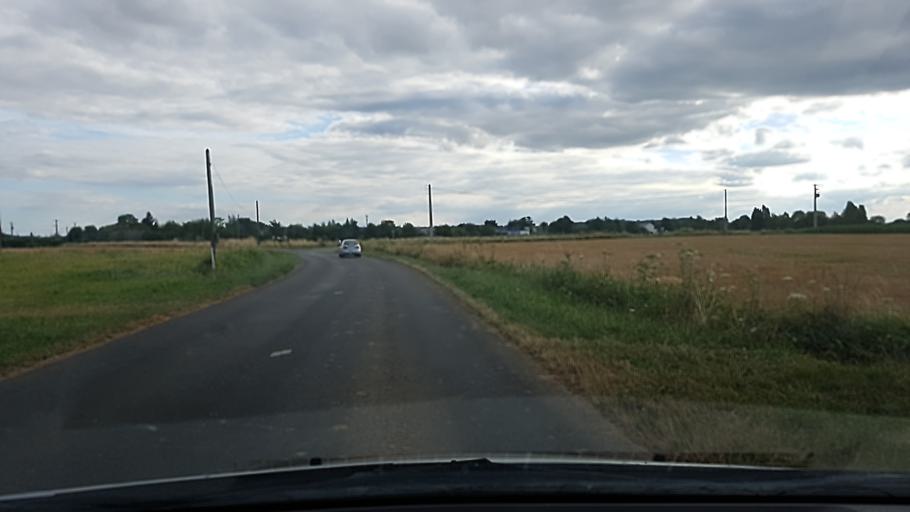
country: FR
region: Pays de la Loire
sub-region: Departement de Maine-et-Loire
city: Saint-Mathurin-sur-Loire
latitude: 47.4213
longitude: -0.3082
